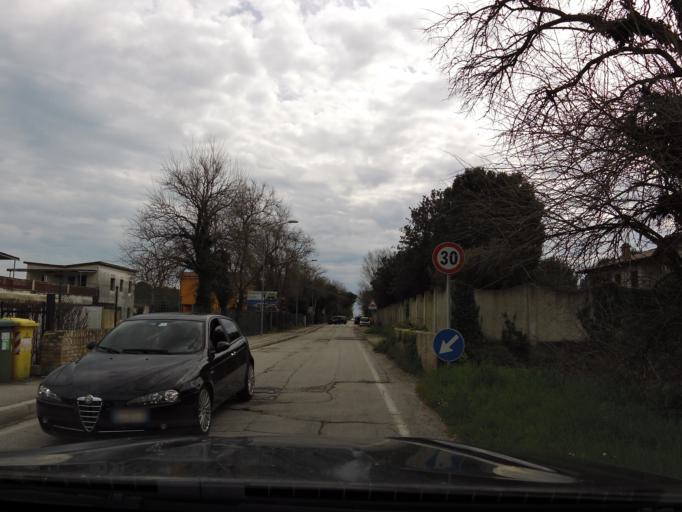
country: IT
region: The Marches
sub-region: Provincia di Macerata
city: Porto Recanati
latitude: 43.4177
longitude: 13.6719
